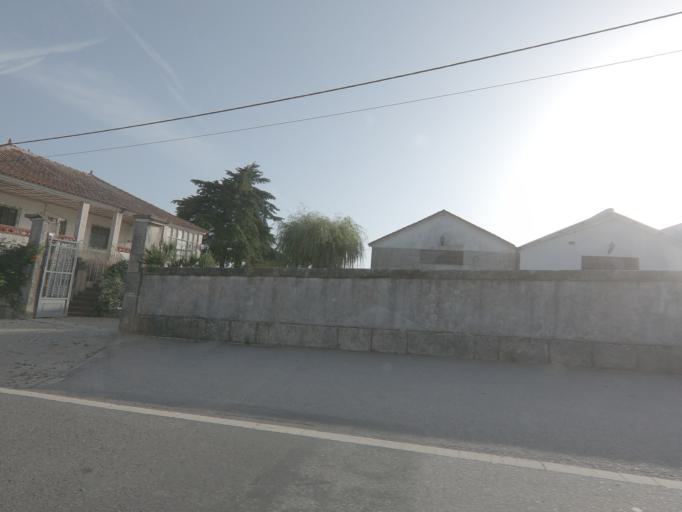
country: PT
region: Vila Real
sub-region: Sabrosa
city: Sabrosa
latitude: 41.2602
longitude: -7.4694
